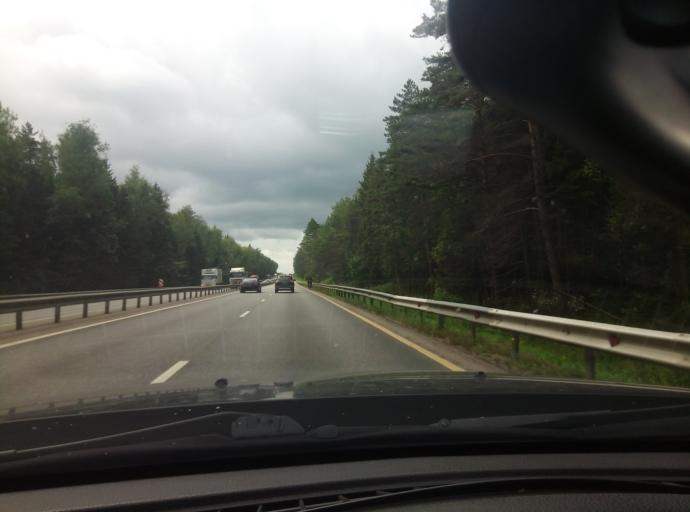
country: RU
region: Kaluga
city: Maloyaroslavets
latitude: 55.0191
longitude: 36.5585
